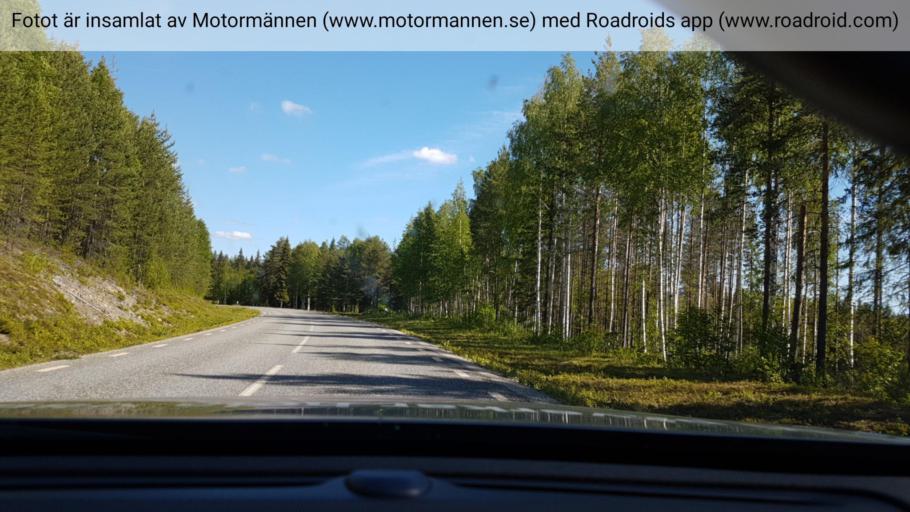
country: SE
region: Vaesterbotten
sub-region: Lycksele Kommun
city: Lycksele
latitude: 64.6045
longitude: 18.5096
